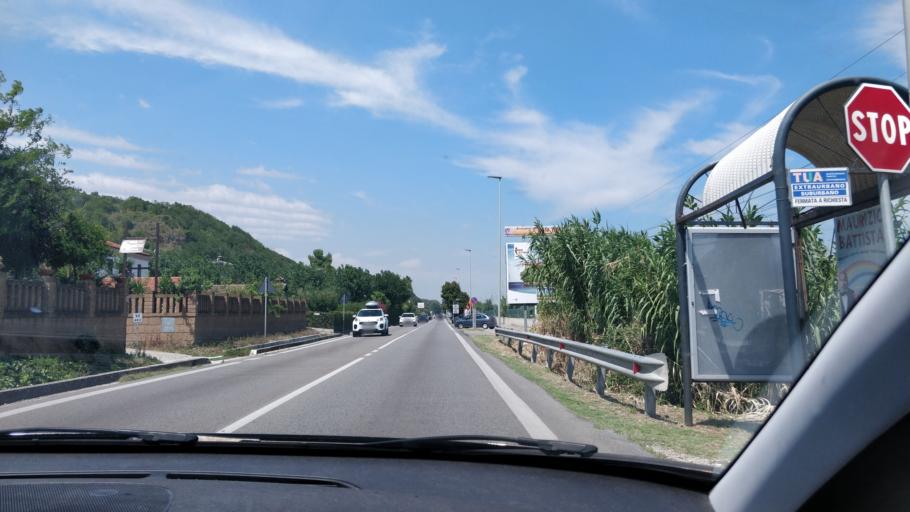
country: IT
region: Abruzzo
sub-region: Provincia di Chieti
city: Tollo
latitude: 42.3813
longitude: 14.3642
